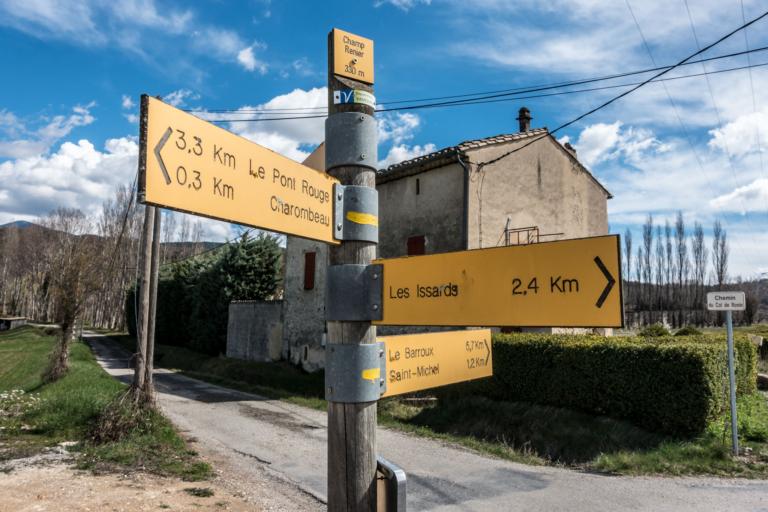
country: FR
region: Provence-Alpes-Cote d'Azur
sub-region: Departement du Vaucluse
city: Malaucene
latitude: 44.1692
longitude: 5.1191
